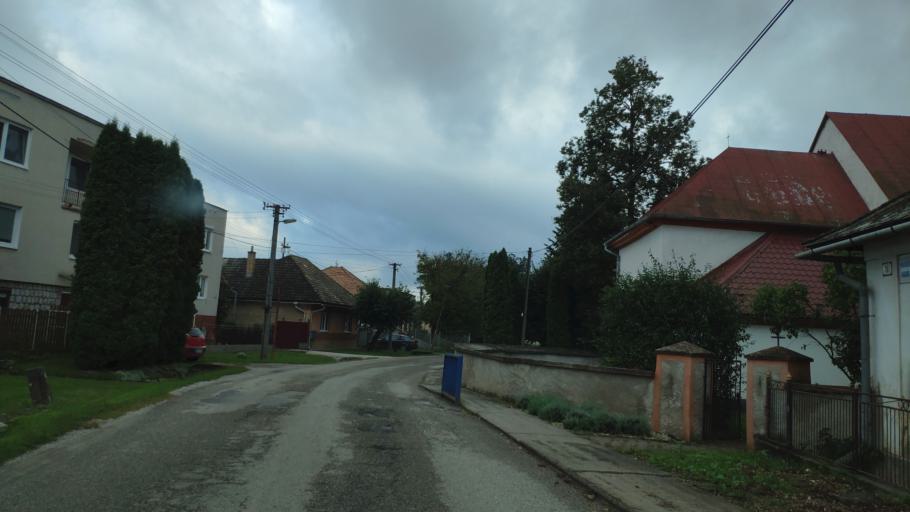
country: SK
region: Kosicky
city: Moldava nad Bodvou
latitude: 48.5791
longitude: 20.8874
